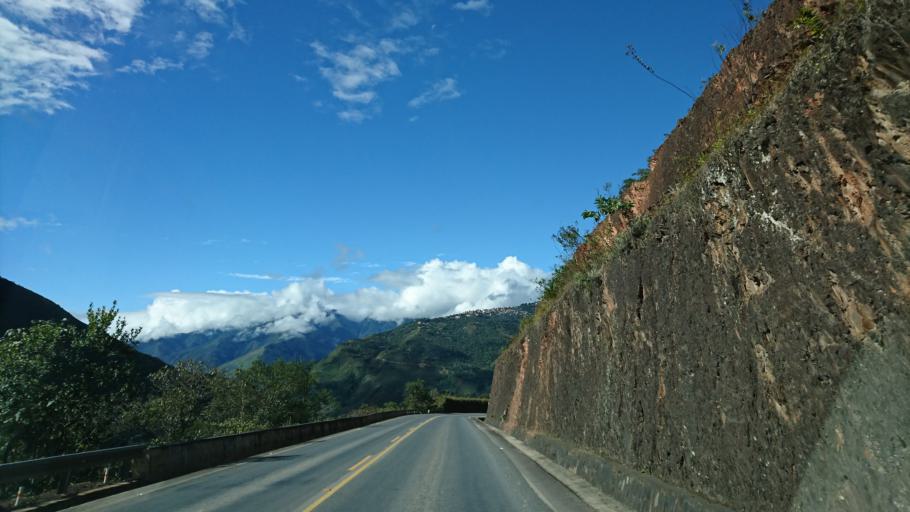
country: BO
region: La Paz
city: Coroico
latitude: -16.2035
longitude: -67.7653
